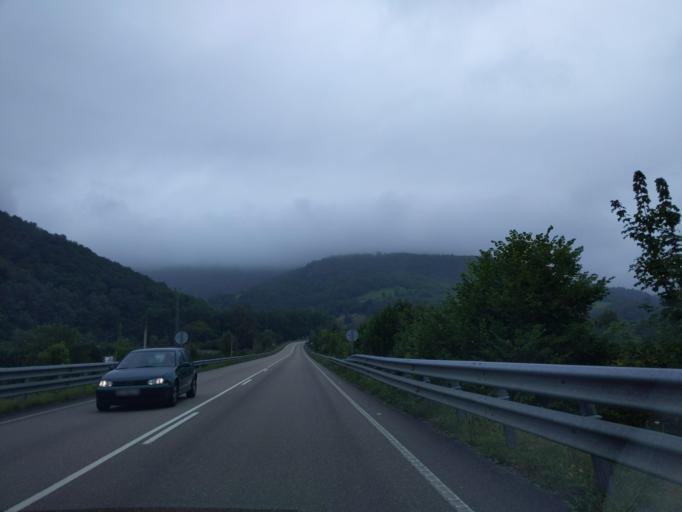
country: ES
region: Asturias
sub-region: Province of Asturias
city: Pola de Laviana
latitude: 43.2345
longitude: -5.5272
